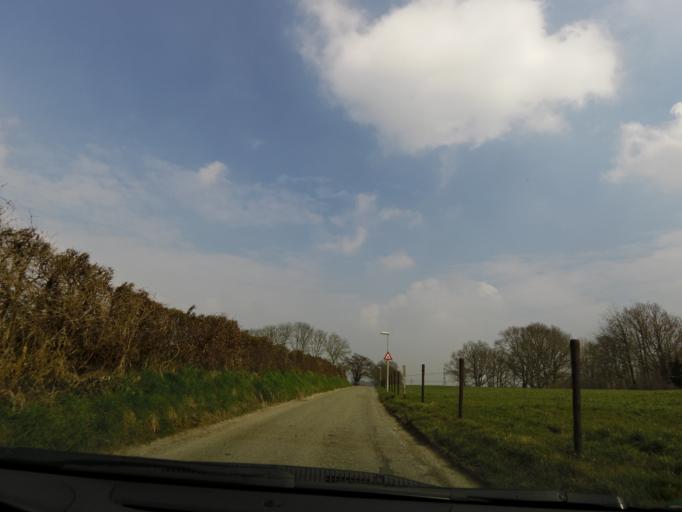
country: NL
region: Limburg
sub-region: Valkenburg aan de Geul
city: Schin op Geul
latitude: 50.8574
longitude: 5.8744
